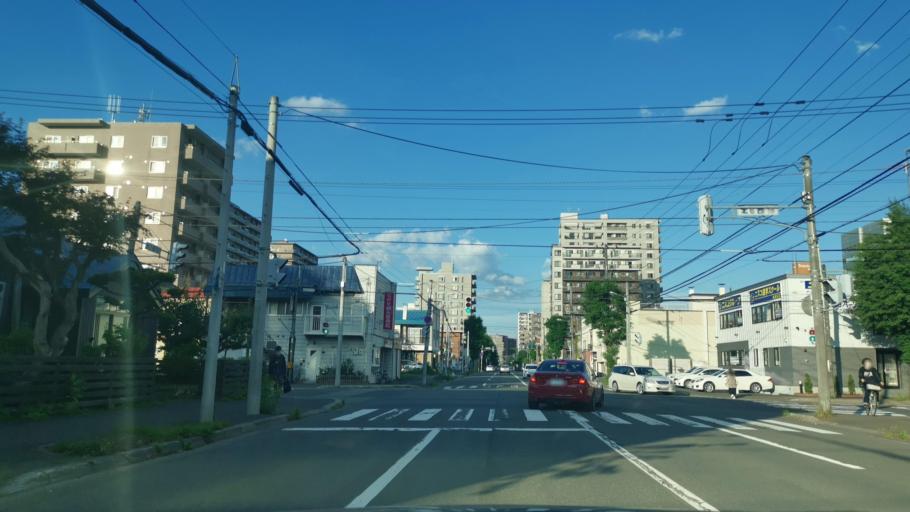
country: JP
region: Hokkaido
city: Sapporo
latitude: 43.0660
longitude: 141.3276
